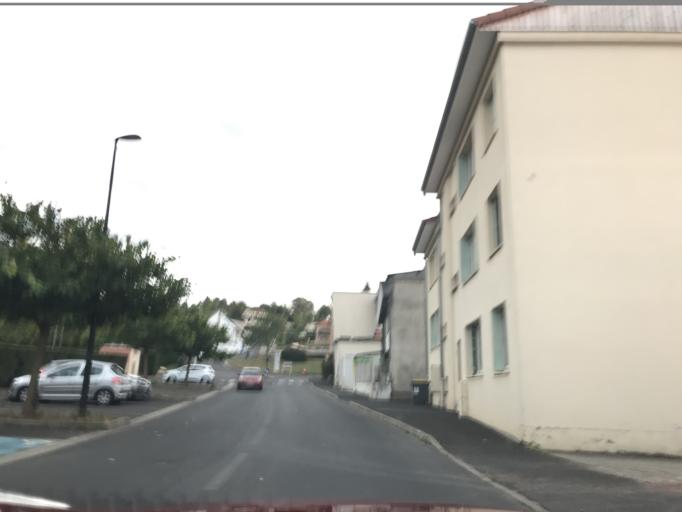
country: FR
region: Auvergne
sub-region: Departement du Puy-de-Dome
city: Thiers
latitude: 45.8494
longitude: 3.5390
